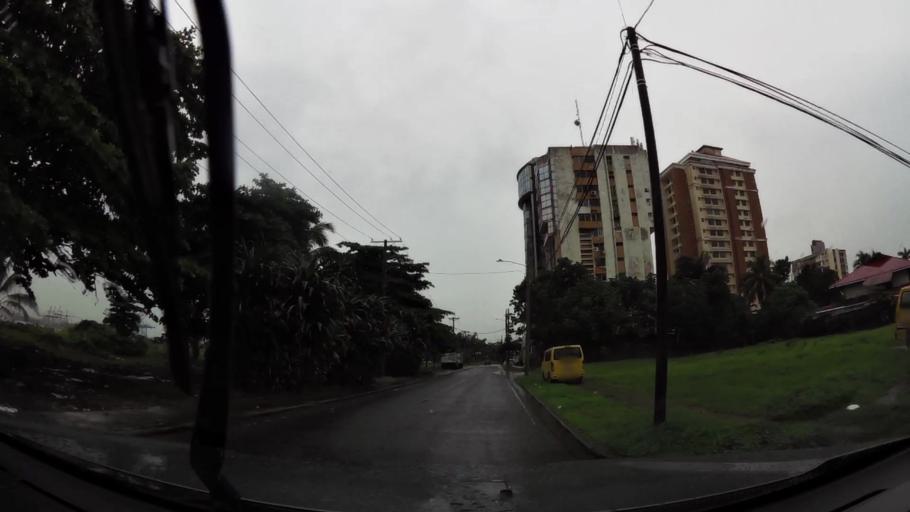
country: PA
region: Colon
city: Colon
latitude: 9.3661
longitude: -79.9002
